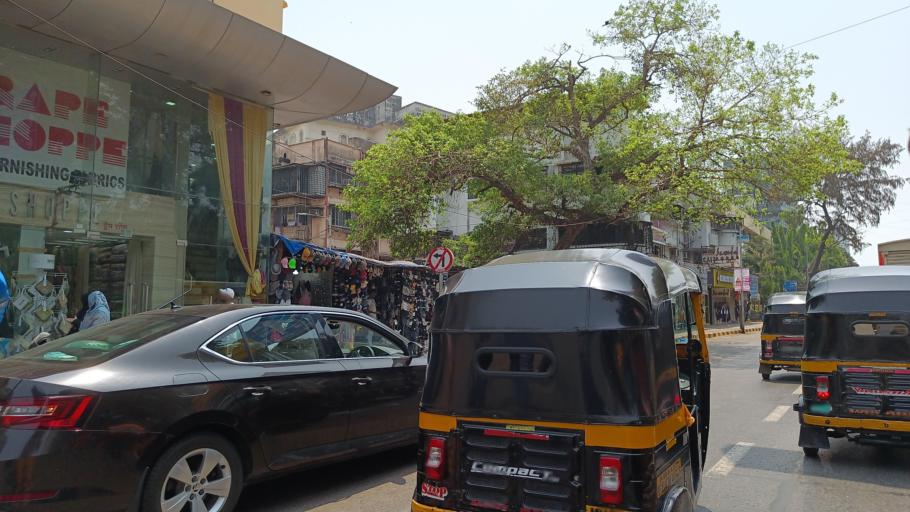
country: IN
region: Maharashtra
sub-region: Mumbai Suburban
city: Mumbai
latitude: 19.0650
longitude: 72.8346
